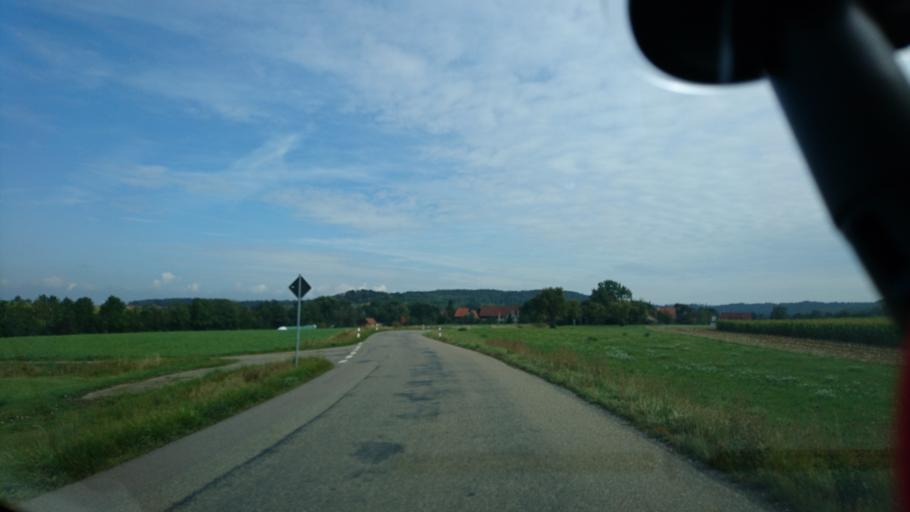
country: DE
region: Baden-Wuerttemberg
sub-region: Regierungsbezirk Stuttgart
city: Ilshofen
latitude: 49.1276
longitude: 9.9268
